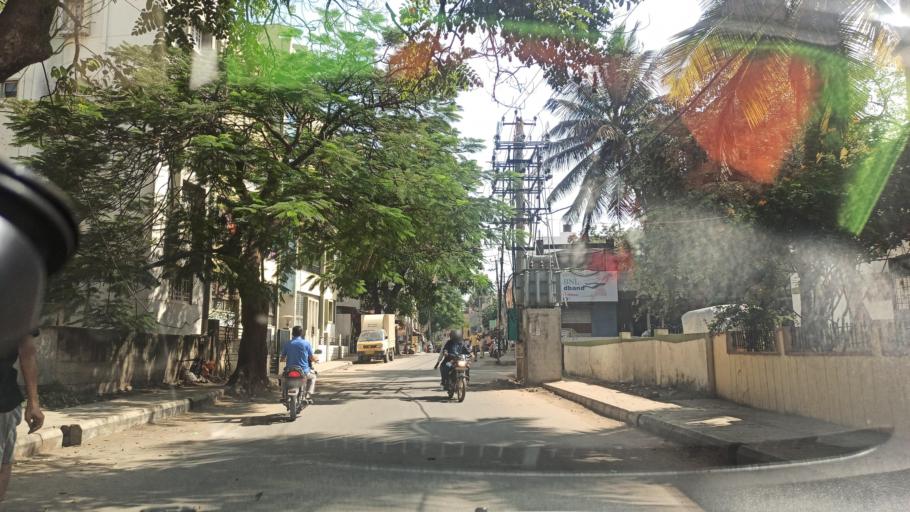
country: IN
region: Karnataka
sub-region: Bangalore Urban
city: Yelahanka
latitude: 13.0425
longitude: 77.5750
